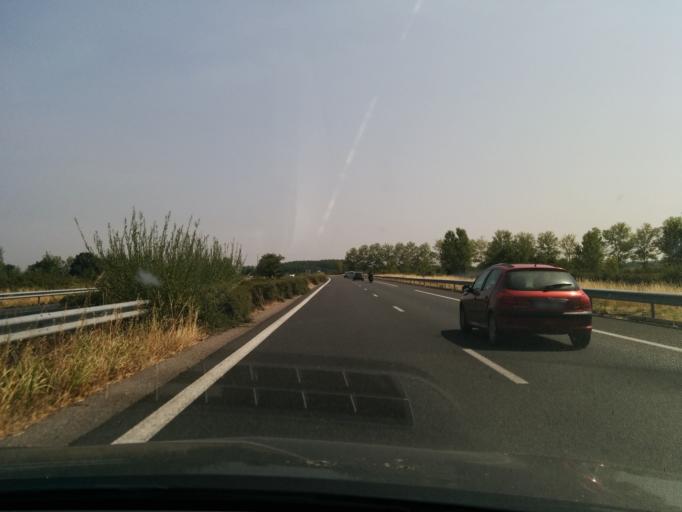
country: FR
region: Midi-Pyrenees
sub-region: Departement du Tarn
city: Marssac-sur-Tarn
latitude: 43.8943
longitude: 2.0265
